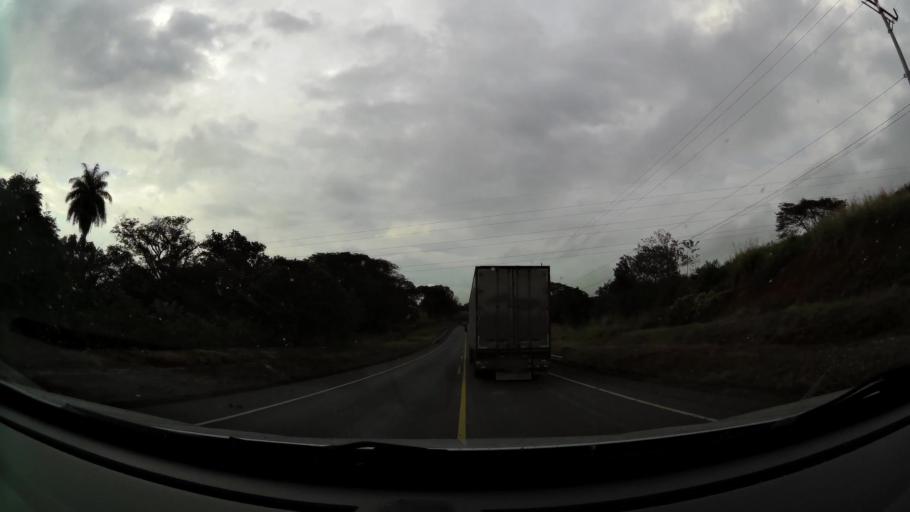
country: CR
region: Alajuela
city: Carrillos
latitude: 9.9681
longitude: -84.2804
